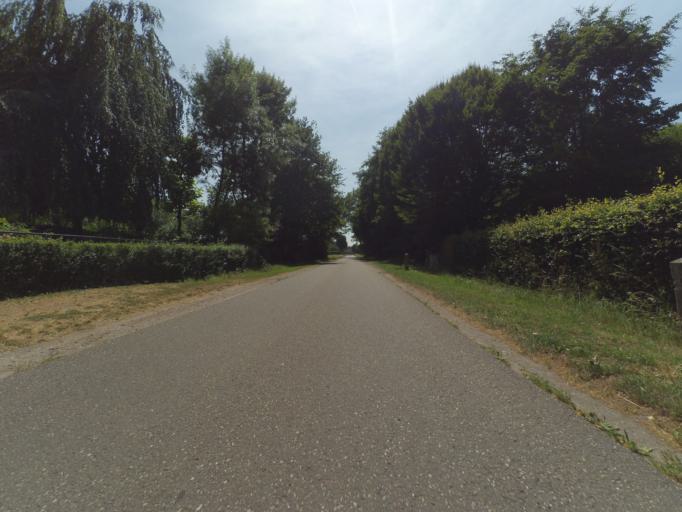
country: NL
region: North Brabant
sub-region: Gemeente Steenbergen
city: Welberg
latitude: 51.5317
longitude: 4.3535
